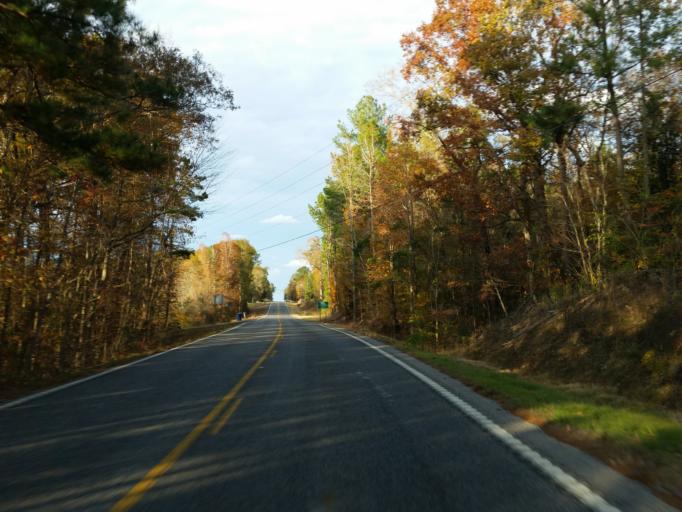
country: US
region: Mississippi
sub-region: Clarke County
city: Stonewall
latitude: 32.2241
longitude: -88.7730
